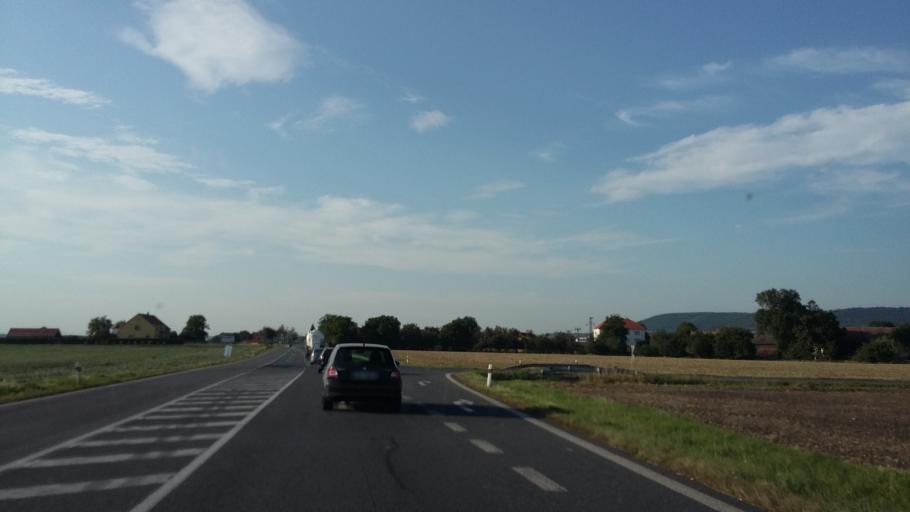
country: CZ
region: Central Bohemia
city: Lustenice
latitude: 50.3482
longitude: 14.9152
